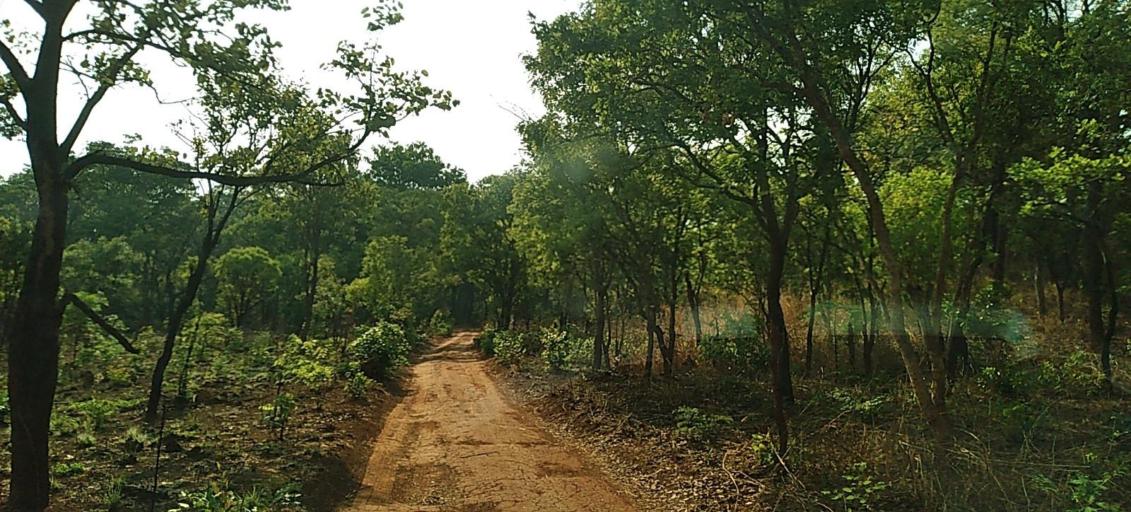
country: ZM
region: North-Western
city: Solwezi
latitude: -12.0599
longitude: 26.1683
